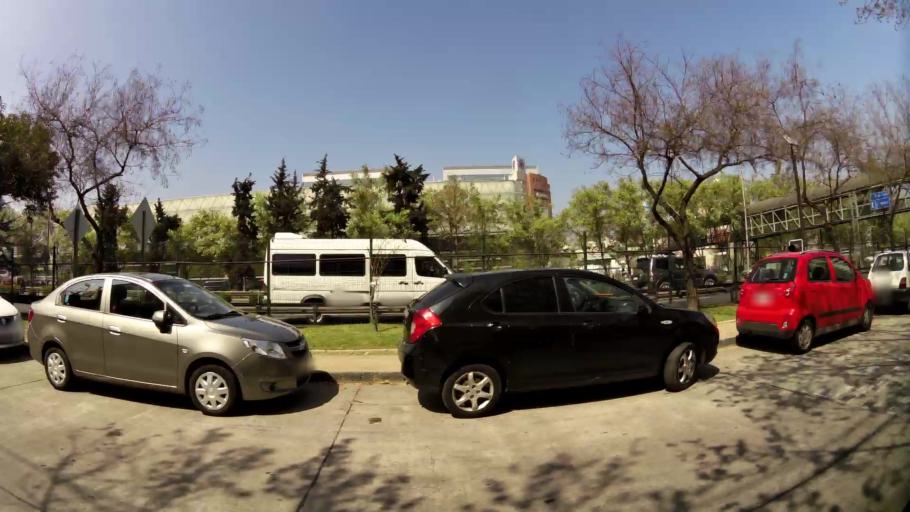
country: CL
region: Santiago Metropolitan
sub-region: Provincia de Santiago
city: Villa Presidente Frei, Nunoa, Santiago, Chile
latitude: -33.4007
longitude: -70.5788
